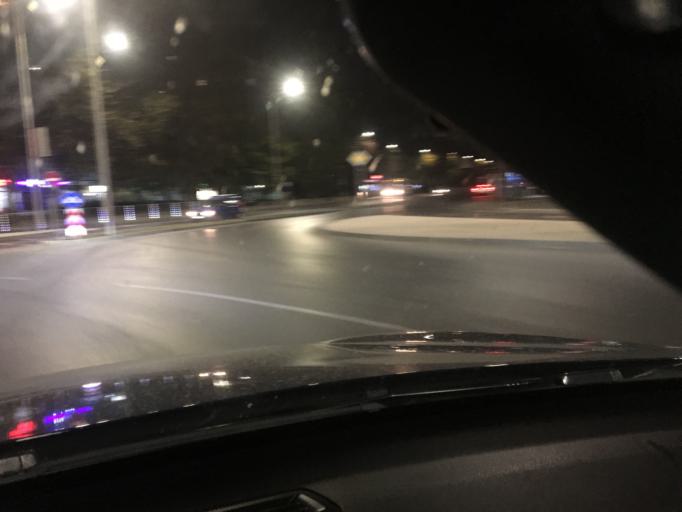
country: BG
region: Varna
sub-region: Obshtina Varna
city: Varna
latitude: 43.2153
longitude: 27.8976
